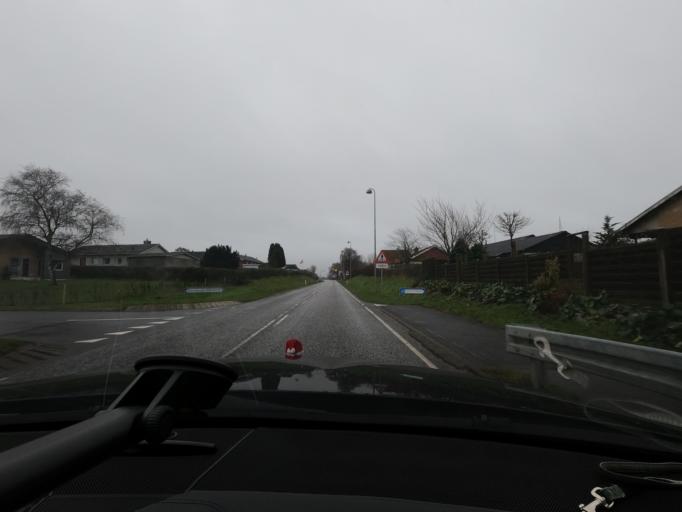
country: DK
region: South Denmark
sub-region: Sonderborg Kommune
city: Broager
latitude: 54.9225
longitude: 9.6829
